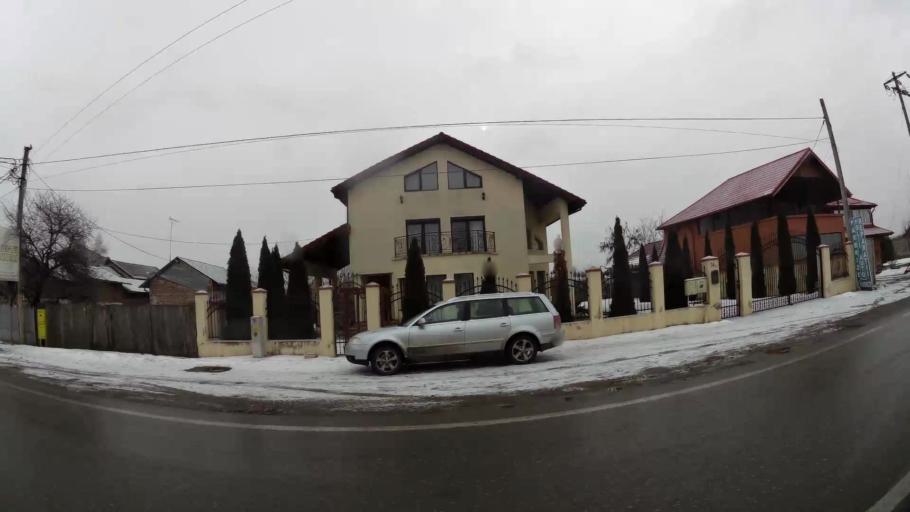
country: RO
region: Dambovita
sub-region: Comuna Aninoasa
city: Viforata
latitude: 44.9477
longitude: 25.4700
